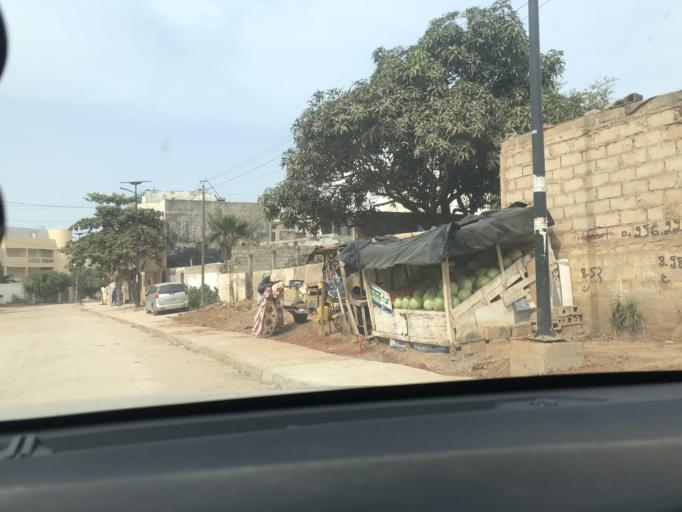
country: SN
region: Dakar
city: Mermoz Boabab
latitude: 14.7296
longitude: -17.4977
